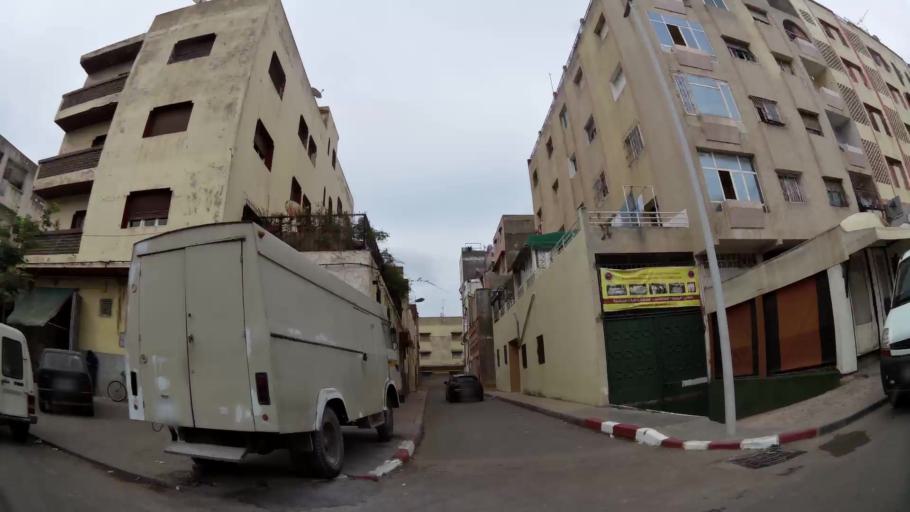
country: MA
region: Rabat-Sale-Zemmour-Zaer
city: Sale
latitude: 34.0407
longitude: -6.8101
